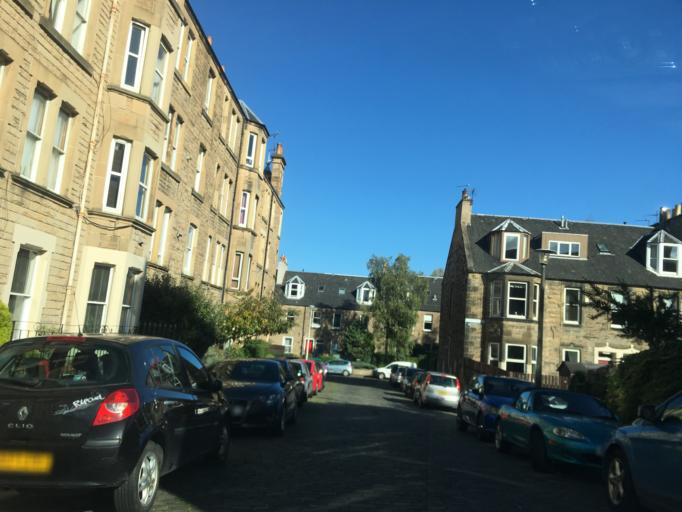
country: GB
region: Scotland
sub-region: Edinburgh
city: Colinton
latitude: 55.9341
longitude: -3.2306
